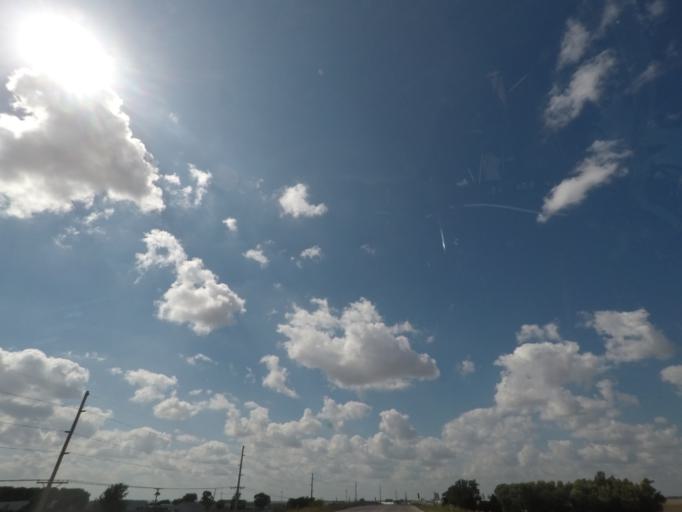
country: US
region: Iowa
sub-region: Story County
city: Nevada
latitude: 42.0228
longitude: -93.4758
